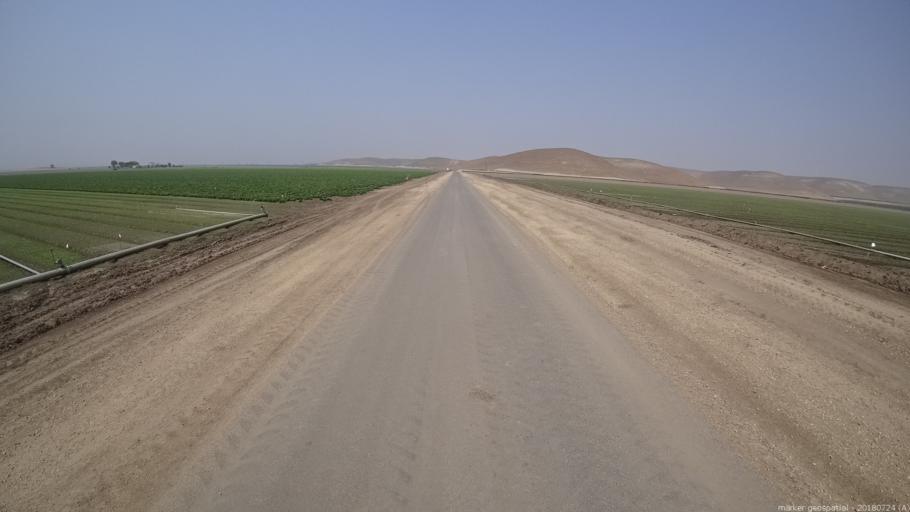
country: US
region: California
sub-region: Monterey County
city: King City
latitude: 36.1723
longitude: -121.0327
